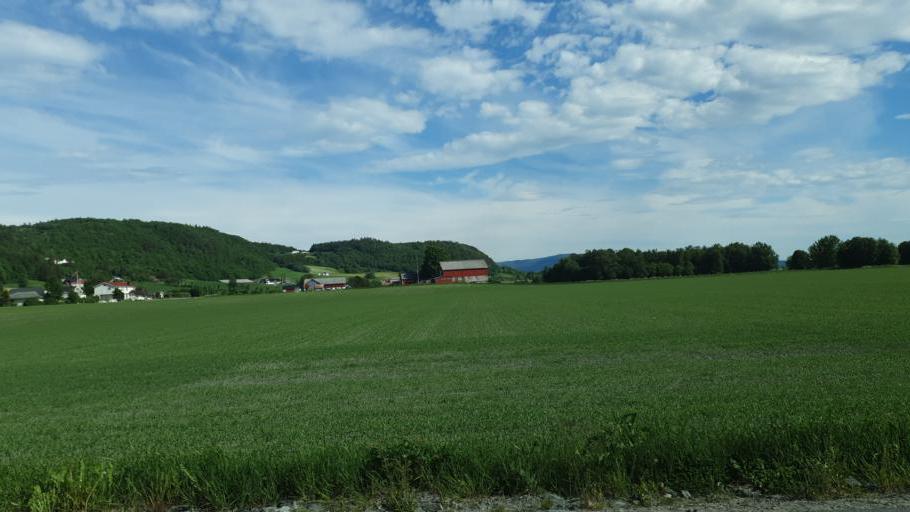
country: NO
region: Sor-Trondelag
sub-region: Rissa
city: Rissa
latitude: 63.5065
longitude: 10.0137
